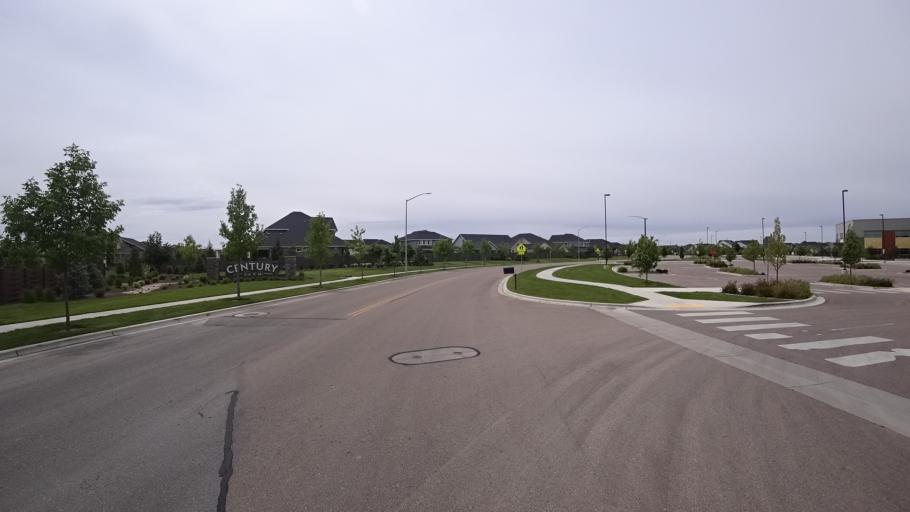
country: US
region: Idaho
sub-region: Ada County
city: Meridian
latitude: 43.5573
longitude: -116.3445
